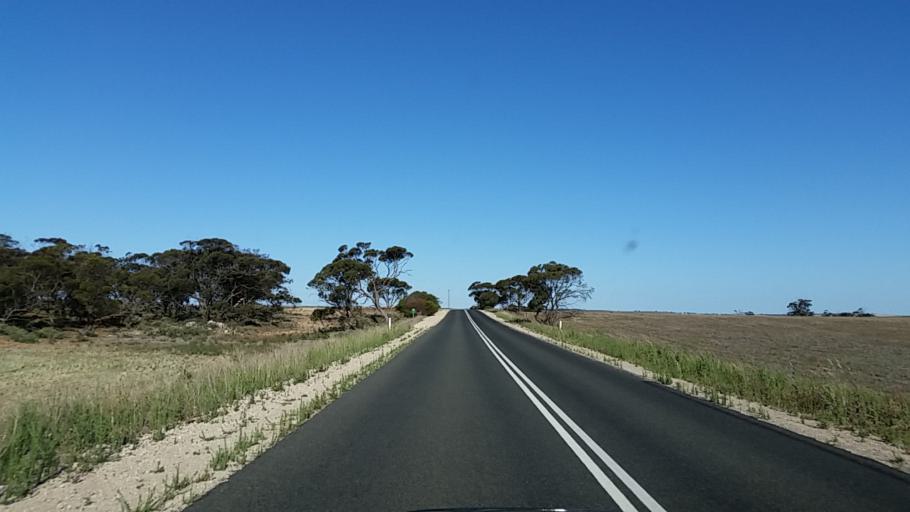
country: AU
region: South Australia
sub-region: Mid Murray
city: Mannum
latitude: -34.7578
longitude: 139.5349
